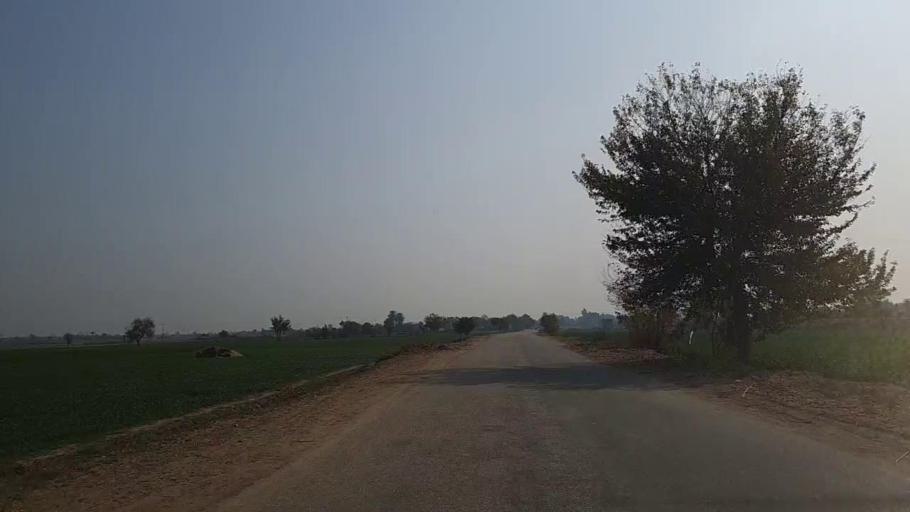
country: PK
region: Sindh
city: Jam Sahib
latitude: 26.3395
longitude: 68.5342
